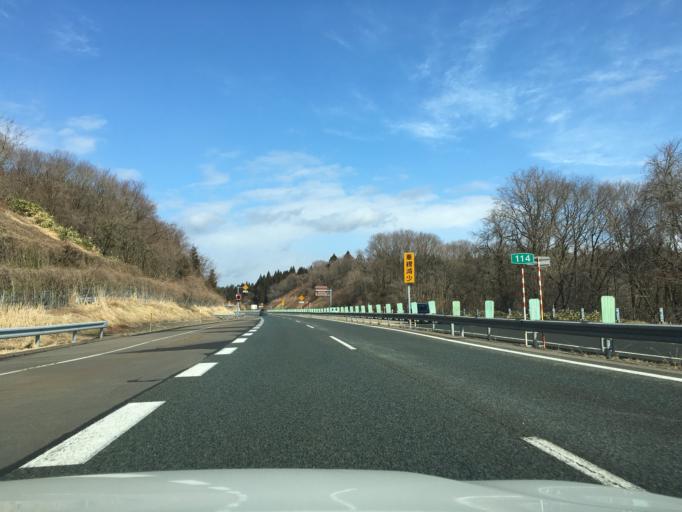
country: JP
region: Akita
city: Akita
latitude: 39.7246
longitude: 140.1810
